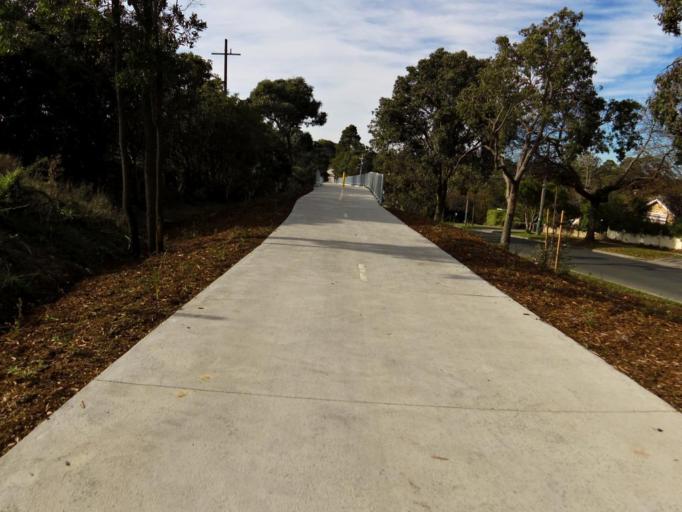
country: AU
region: Victoria
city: Mitcham
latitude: -37.8182
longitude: 145.2008
